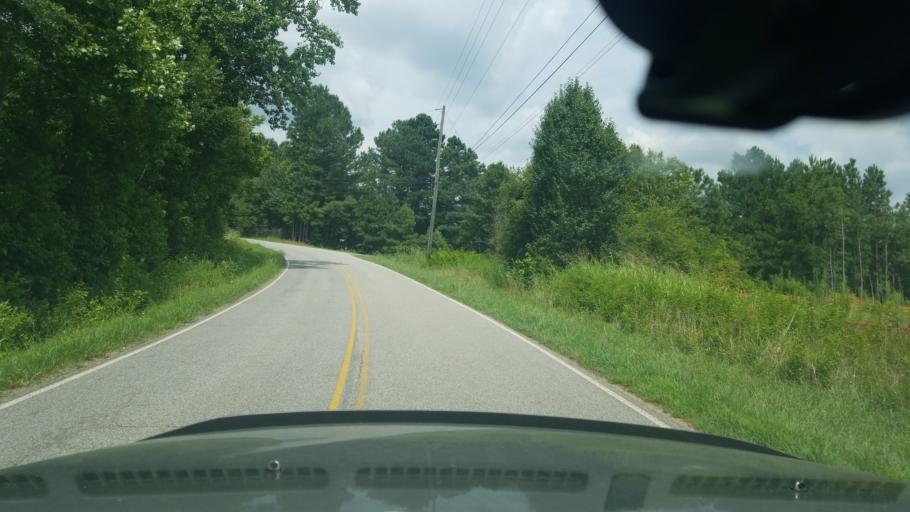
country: US
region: Georgia
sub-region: Forsyth County
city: Cumming
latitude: 34.2712
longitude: -84.2194
